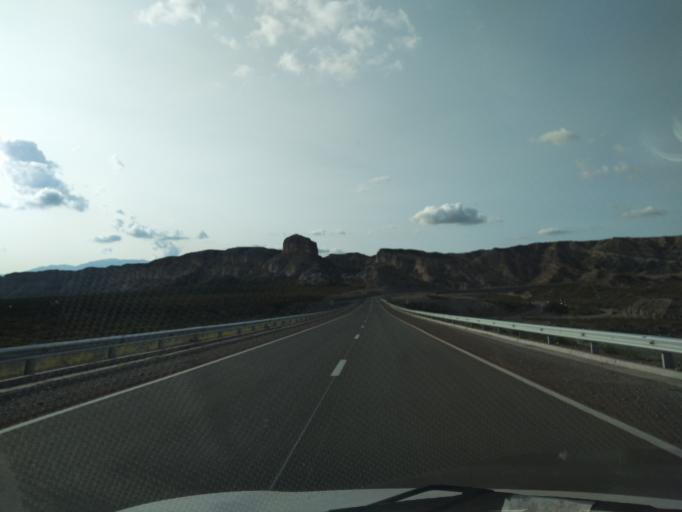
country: AR
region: Mendoza
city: San Rafael
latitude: -34.6414
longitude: -69.1778
